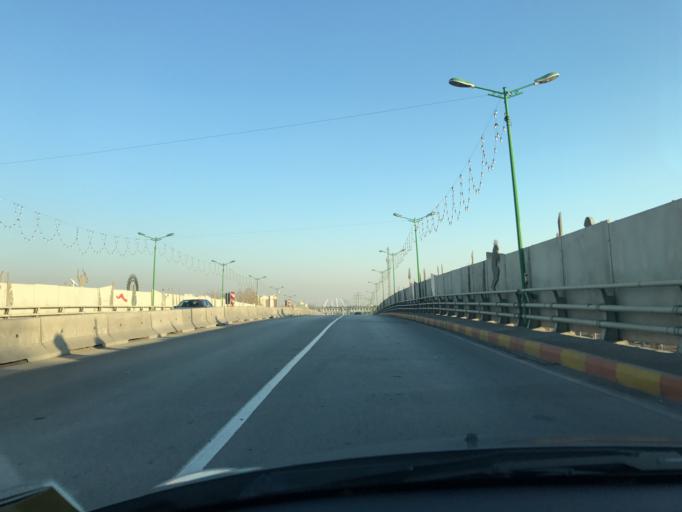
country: IR
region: Qazvin
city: Qazvin
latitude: 36.2887
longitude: 50.0063
